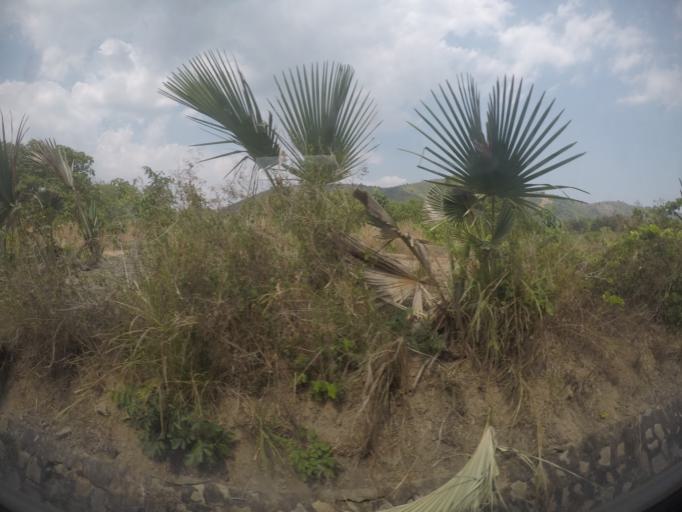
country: VN
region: Binh Thuan
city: Tanh Linh
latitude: 10.9137
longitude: 107.6794
